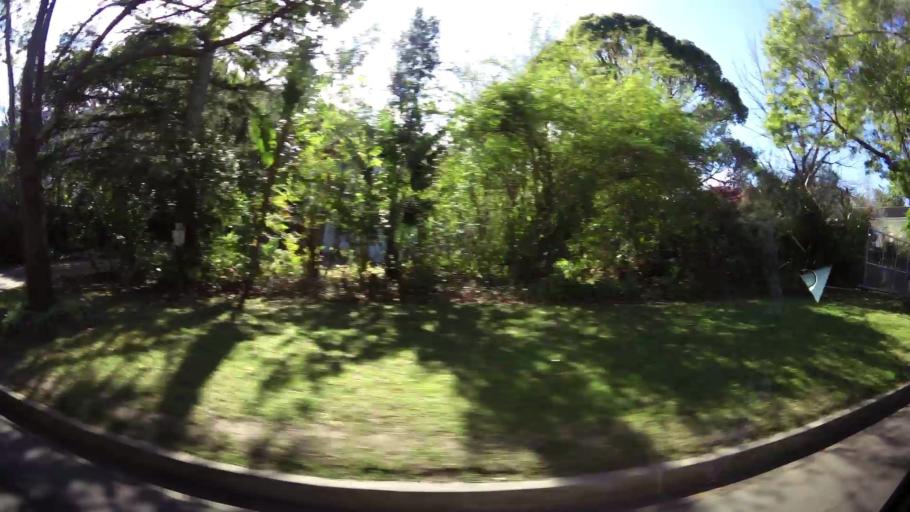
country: ZA
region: Western Cape
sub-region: Eden District Municipality
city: George
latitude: -33.9486
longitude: 22.4613
